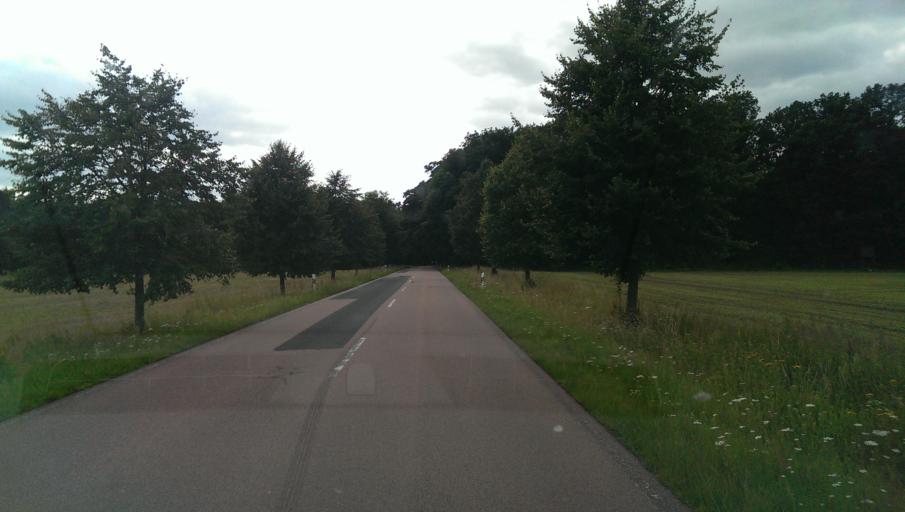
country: DE
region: Saxony-Anhalt
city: Nudersdorf
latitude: 51.9487
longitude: 12.5785
